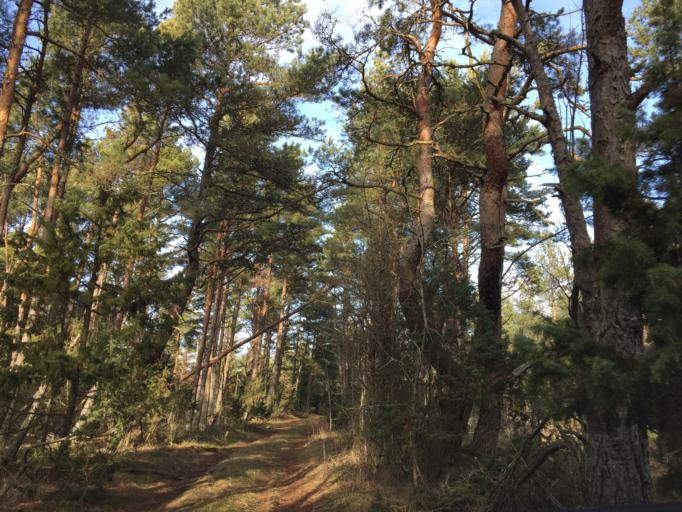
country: EE
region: Saare
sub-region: Kuressaare linn
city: Kuressaare
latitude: 58.3766
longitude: 21.9986
